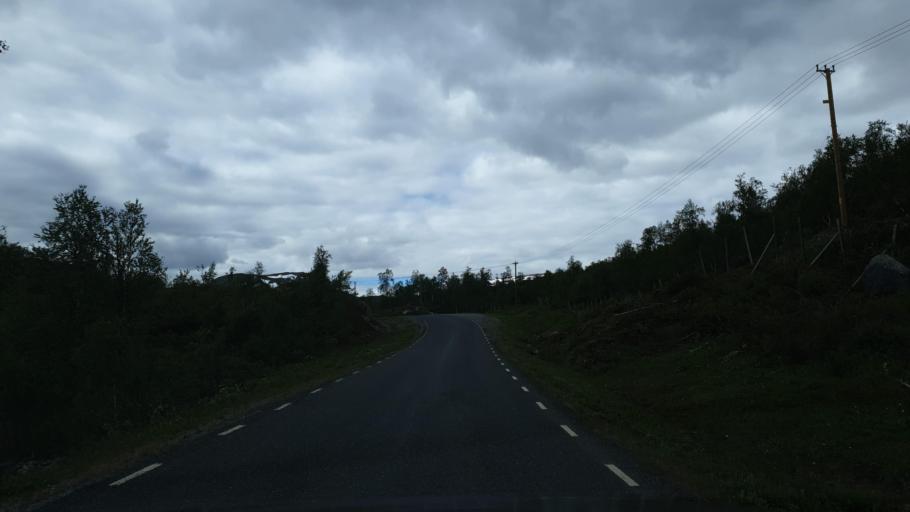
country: NO
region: Nordland
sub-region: Hattfjelldal
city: Hattfjelldal
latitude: 65.4179
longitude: 14.6836
